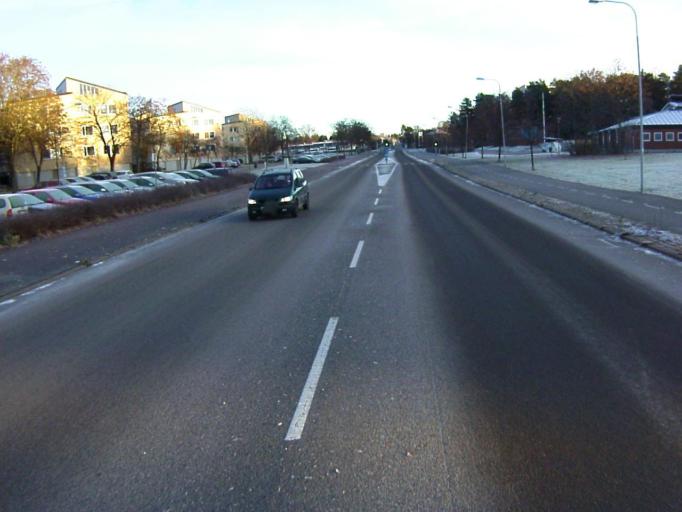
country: SE
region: Soedermanland
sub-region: Eskilstuna Kommun
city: Eskilstuna
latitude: 59.3571
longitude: 16.4896
